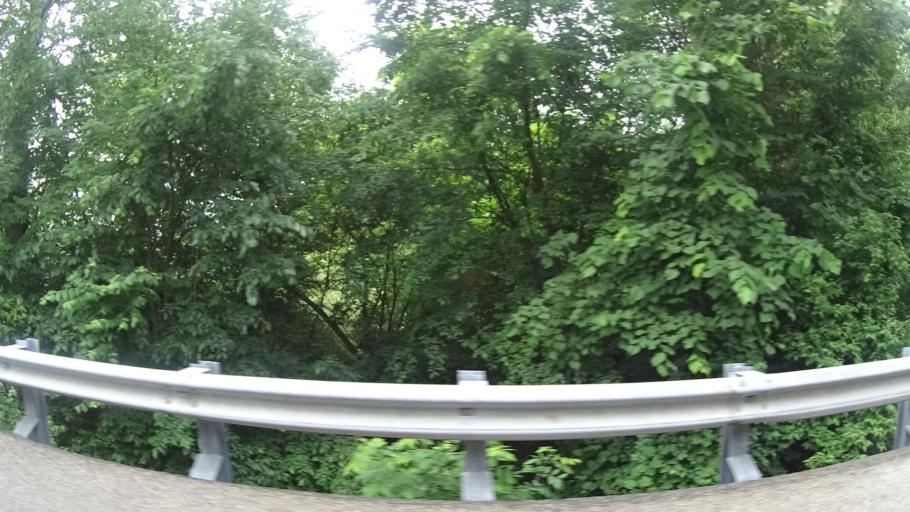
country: US
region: Ohio
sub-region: Erie County
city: Sandusky
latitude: 41.3548
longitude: -82.7334
